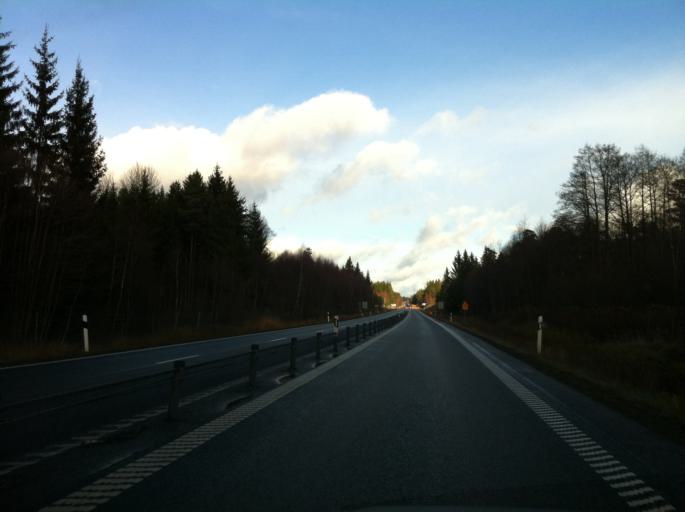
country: SE
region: Skane
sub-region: Osby Kommun
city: Osby
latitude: 56.4112
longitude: 14.0466
